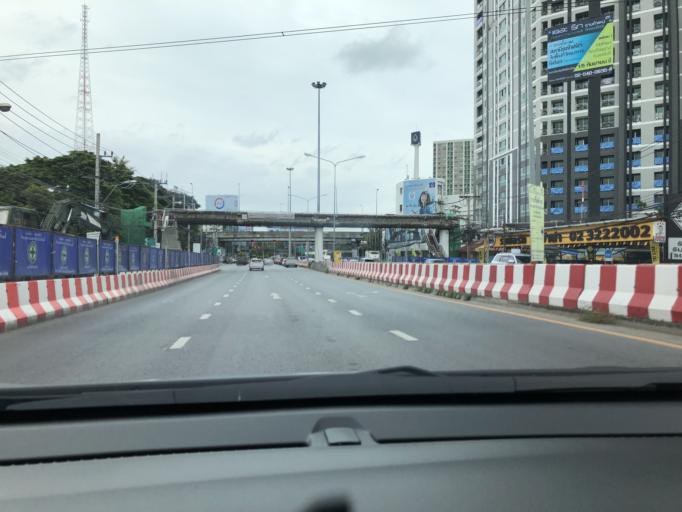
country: TH
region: Bangkok
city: Suan Luang
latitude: 13.7339
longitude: 100.6411
